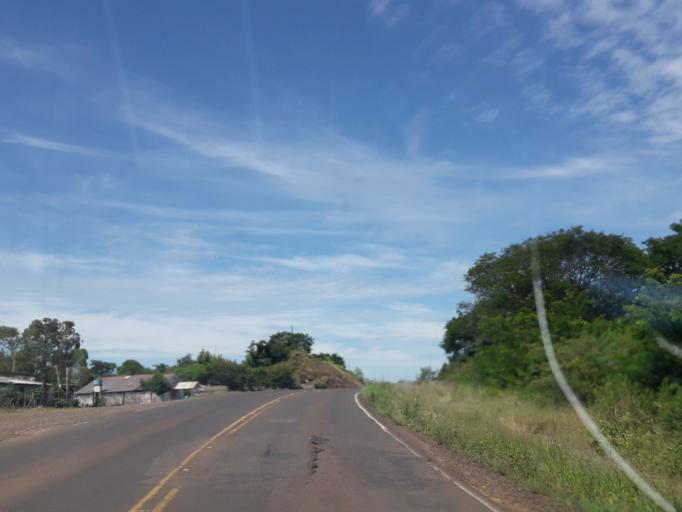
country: AR
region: Misiones
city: Bernardo de Irigoyen
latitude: -26.4961
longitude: -53.5022
